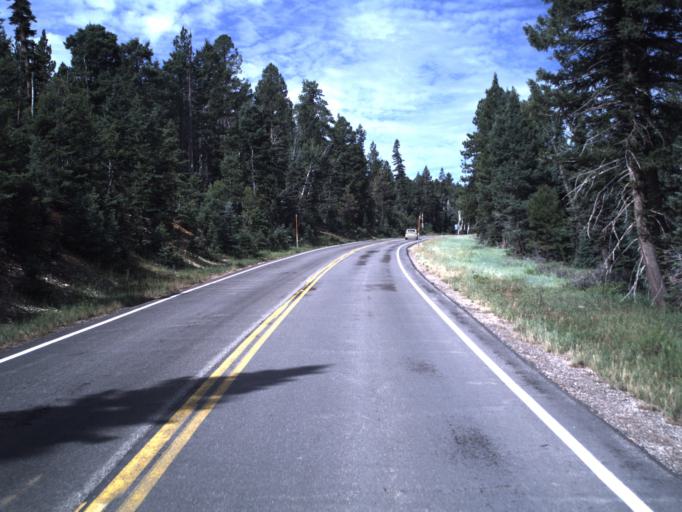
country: US
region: Utah
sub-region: Iron County
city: Parowan
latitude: 37.5179
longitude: -112.6760
